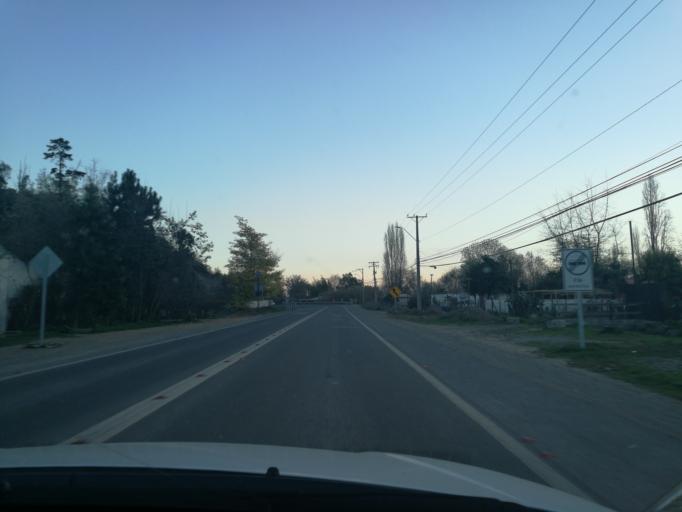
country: CL
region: O'Higgins
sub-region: Provincia de Cachapoal
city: Graneros
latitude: -34.0468
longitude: -70.7263
